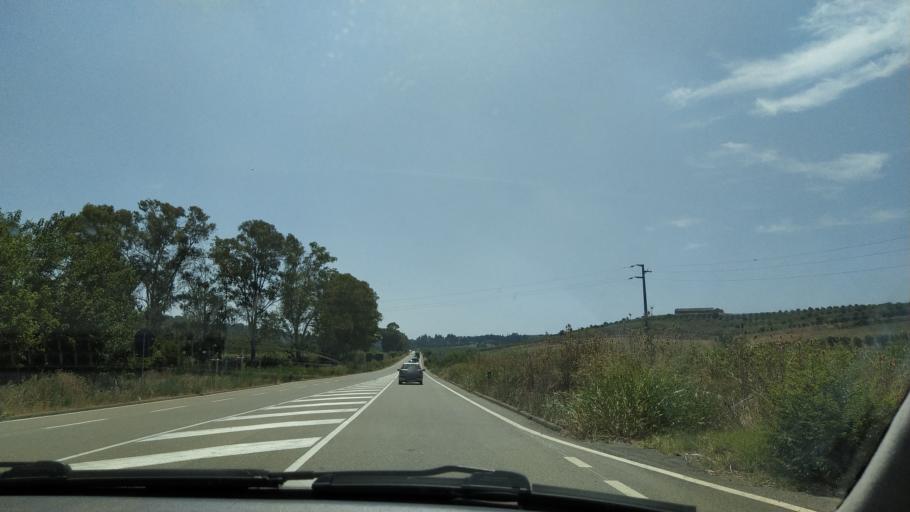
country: IT
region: Basilicate
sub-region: Provincia di Matera
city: Bernalda
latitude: 40.4434
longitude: 16.7811
